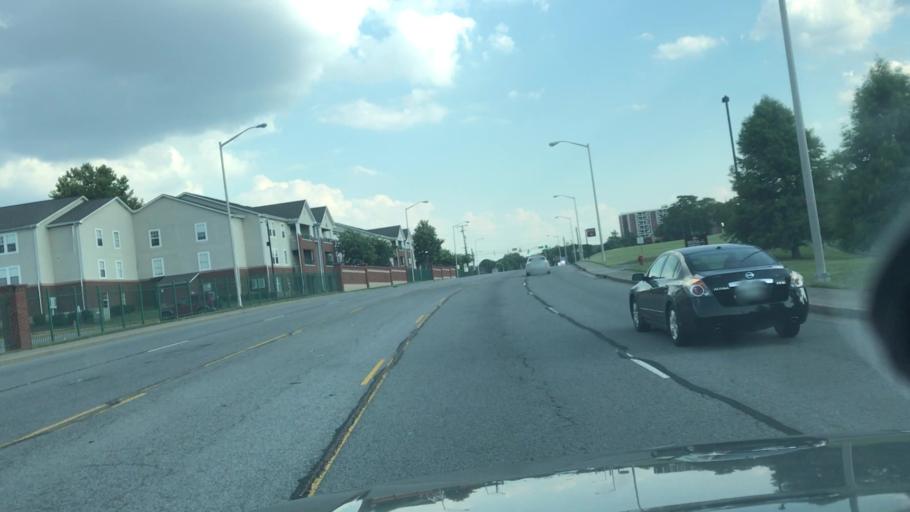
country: US
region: Tennessee
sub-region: Davidson County
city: Nashville
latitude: 36.1718
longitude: -86.8215
